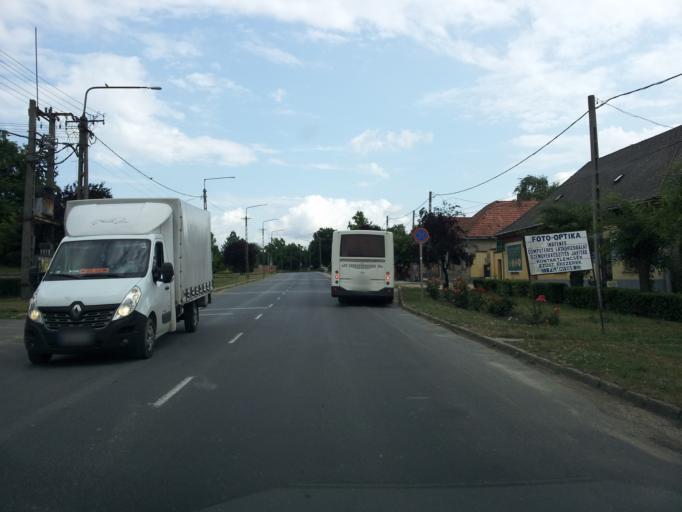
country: HU
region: Fejer
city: Enying
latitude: 46.9288
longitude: 18.2435
